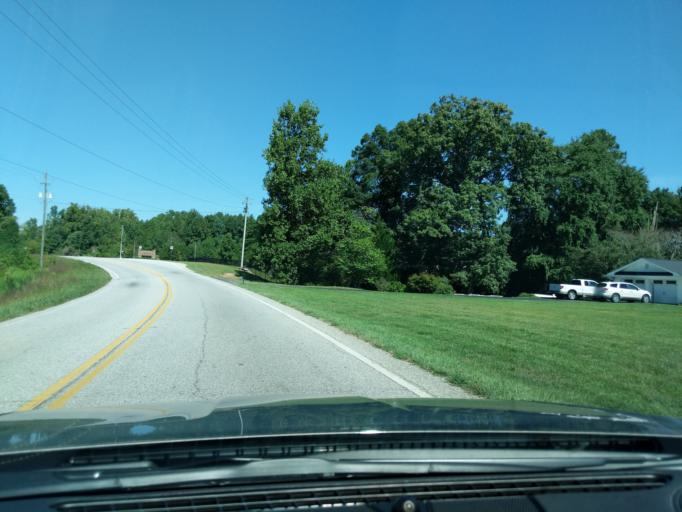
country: US
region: Georgia
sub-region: Habersham County
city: Demorest
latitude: 34.5664
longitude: -83.5802
